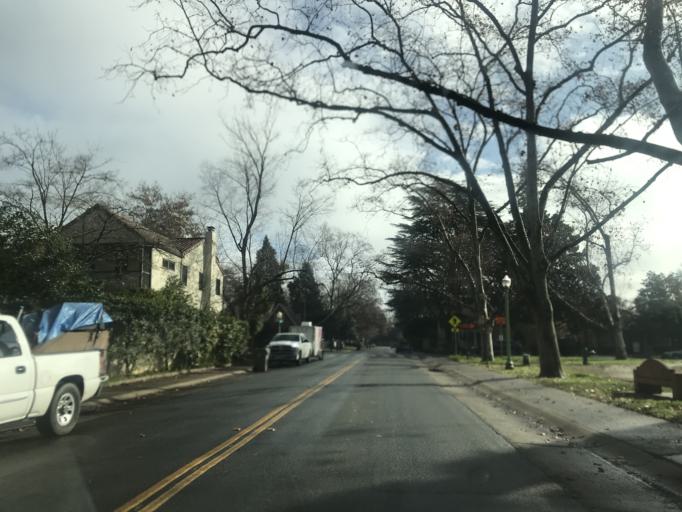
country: US
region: California
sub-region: Sacramento County
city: Sacramento
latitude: 38.5769
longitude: -121.4579
